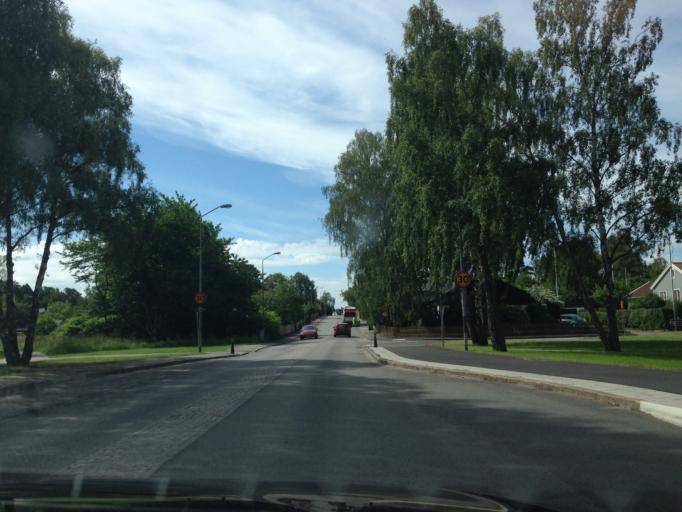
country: SE
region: Kalmar
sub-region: Kalmar Kommun
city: Kalmar
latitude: 56.6930
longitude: 16.3560
